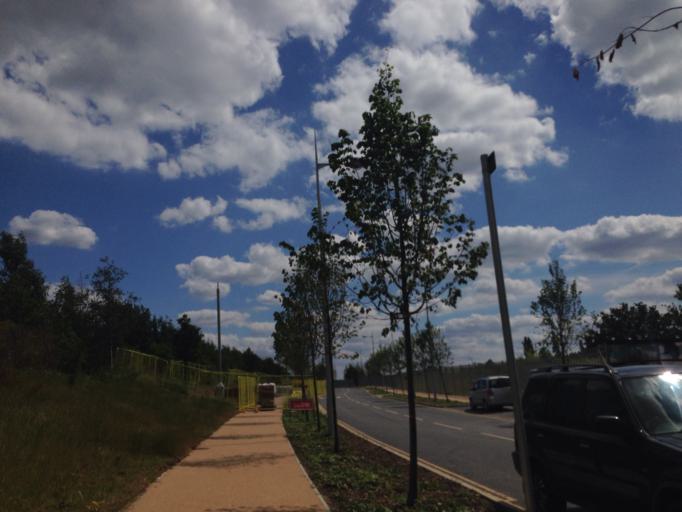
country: GB
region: England
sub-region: Greater London
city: Acton
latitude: 51.5314
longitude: -0.2823
